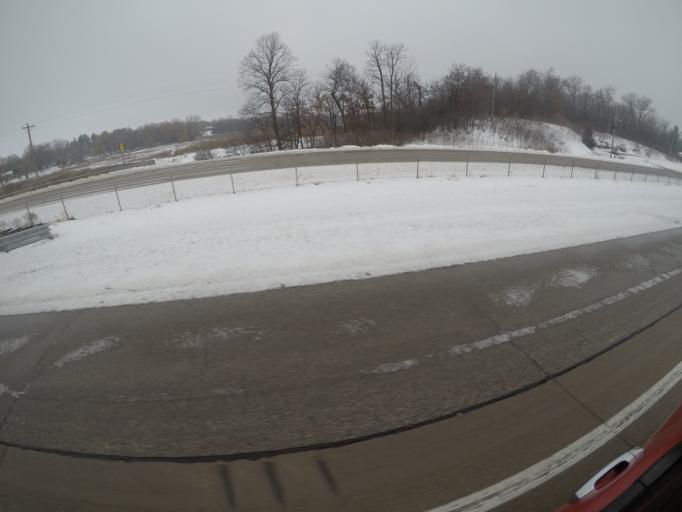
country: US
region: Minnesota
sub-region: Olmsted County
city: Oronoco
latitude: 44.1611
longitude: -92.5410
